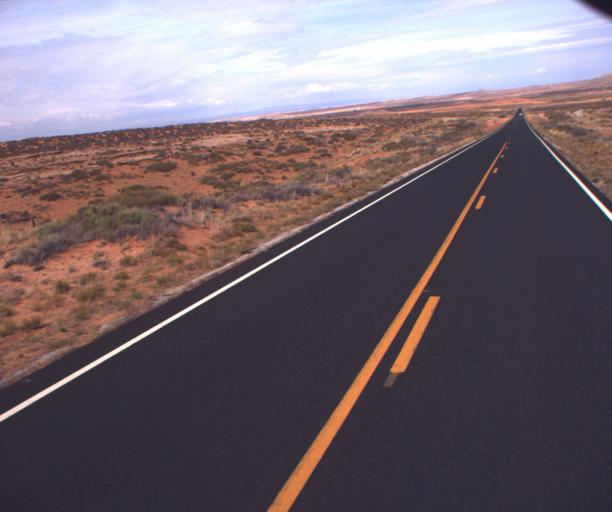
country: US
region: Arizona
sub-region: Apache County
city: Many Farms
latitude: 36.8969
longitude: -109.6259
